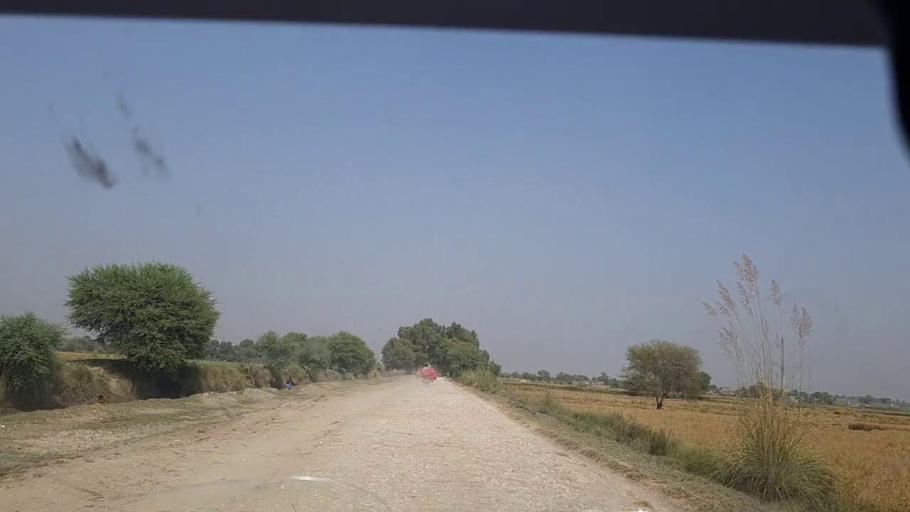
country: PK
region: Sindh
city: Thul
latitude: 28.1082
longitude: 68.6930
